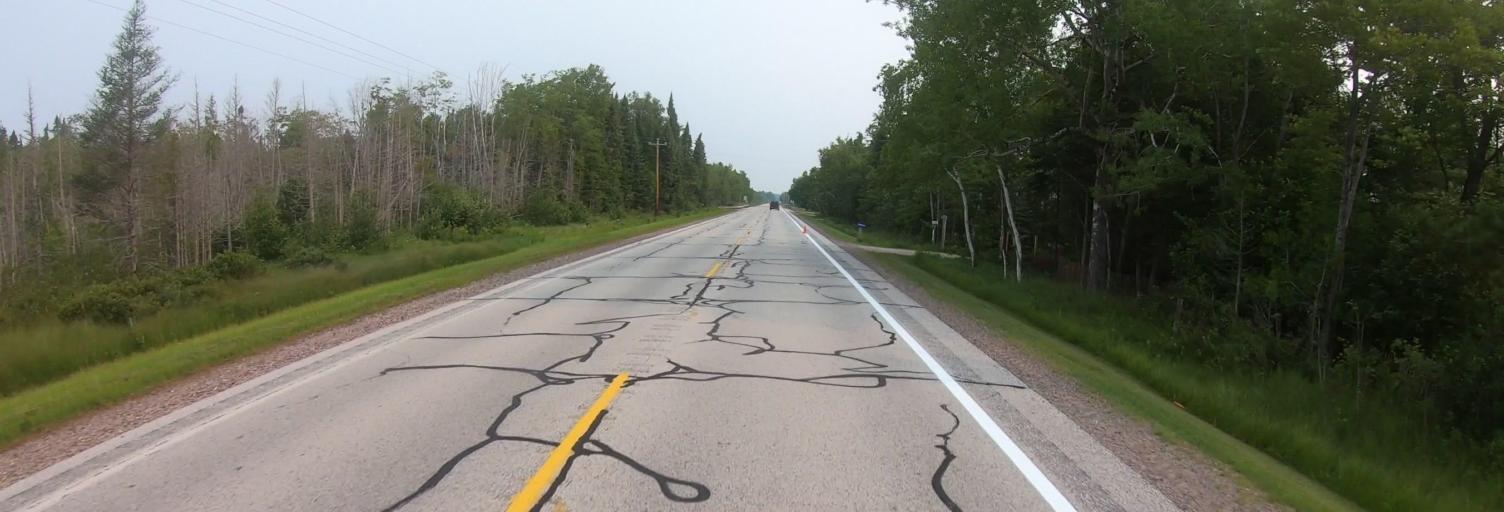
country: US
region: Michigan
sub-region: Luce County
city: Newberry
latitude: 46.5808
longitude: -85.0363
